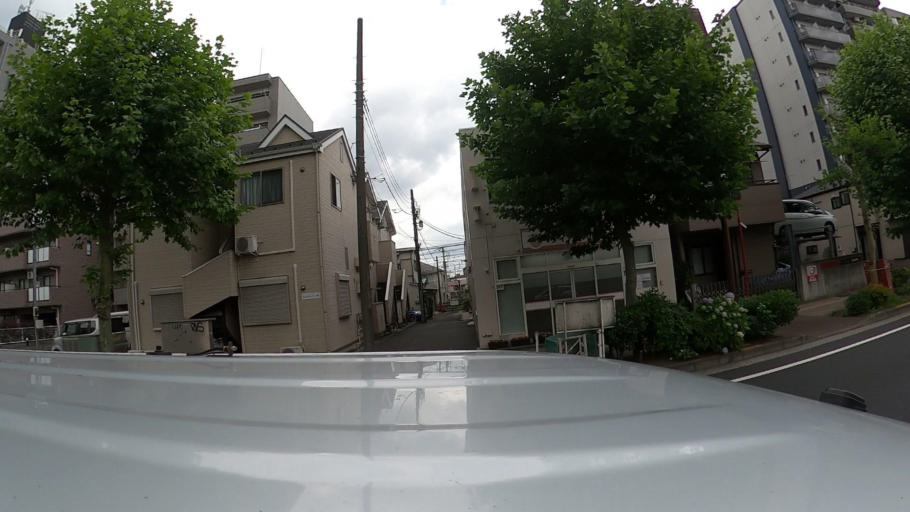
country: JP
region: Kanagawa
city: Yokohama
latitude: 35.4846
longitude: 139.6471
